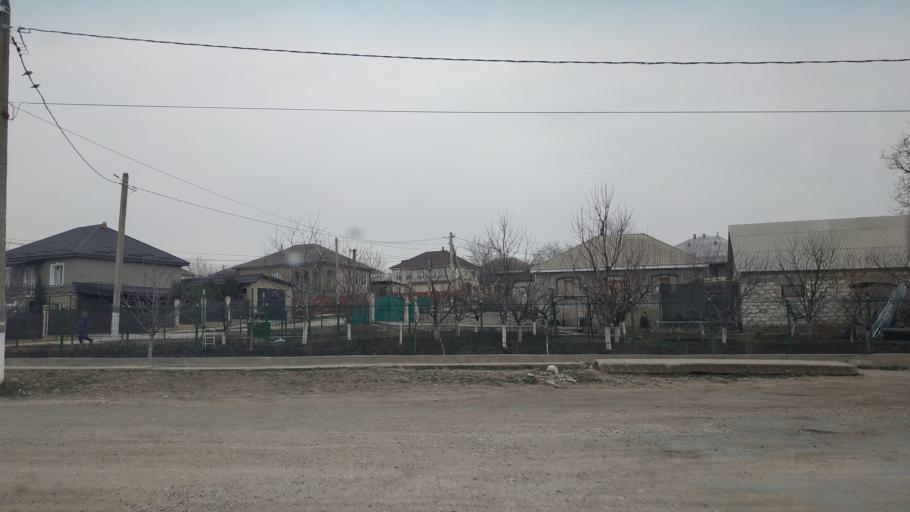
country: MD
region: Chisinau
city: Singera
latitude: 46.8221
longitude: 28.9674
